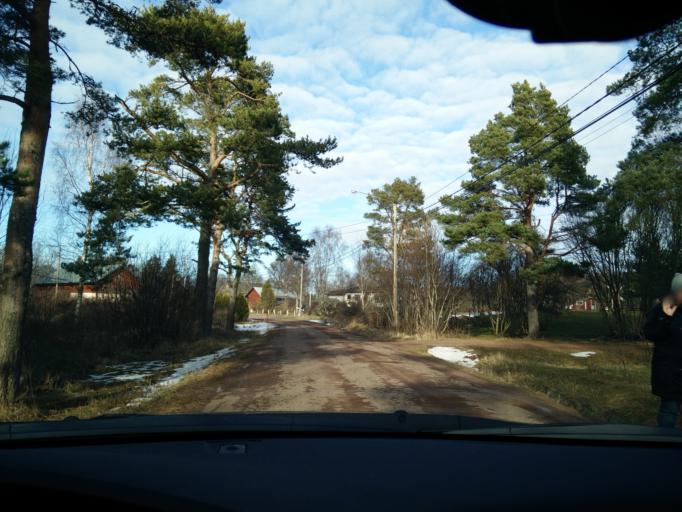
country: AX
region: Alands landsbygd
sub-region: Eckeroe
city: Eckeroe
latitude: 60.2216
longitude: 19.5524
